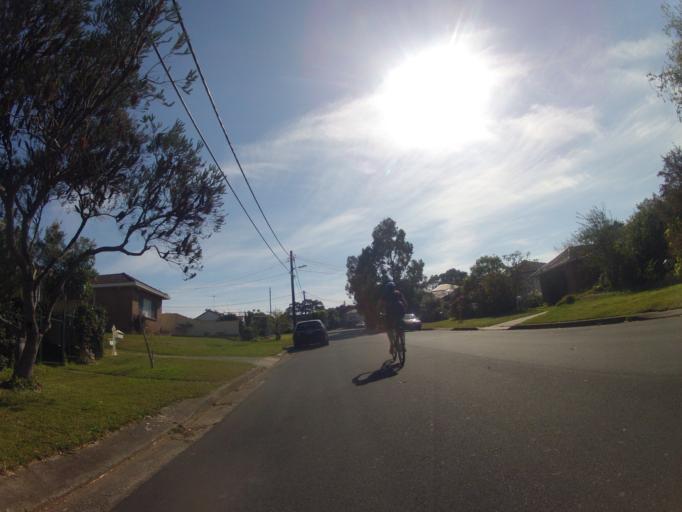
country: AU
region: New South Wales
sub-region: Sutherland Shire
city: Caringbah
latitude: -34.0403
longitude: 151.1148
